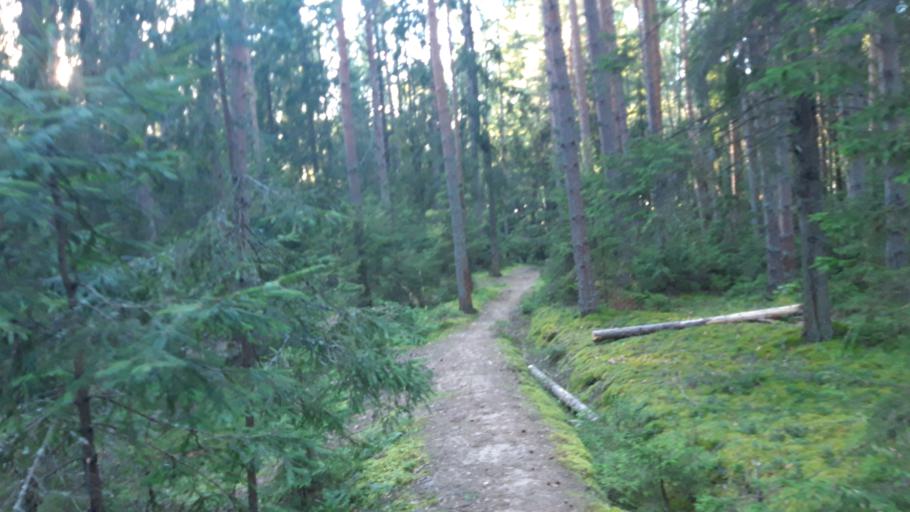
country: RU
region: Tverskaya
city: Konakovo
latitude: 56.6738
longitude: 36.6903
